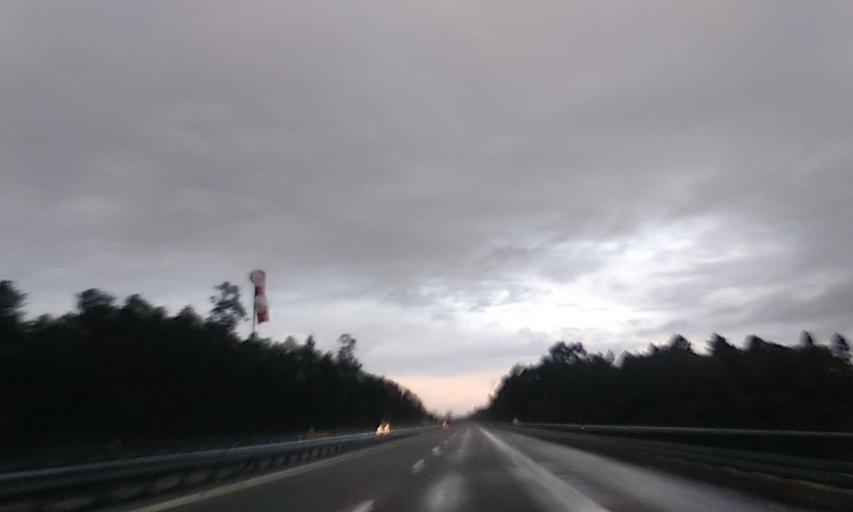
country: PT
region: Viana do Castelo
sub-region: Vila Nova de Cerveira
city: Vila Nova de Cerveira
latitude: 41.8950
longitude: -8.6591
